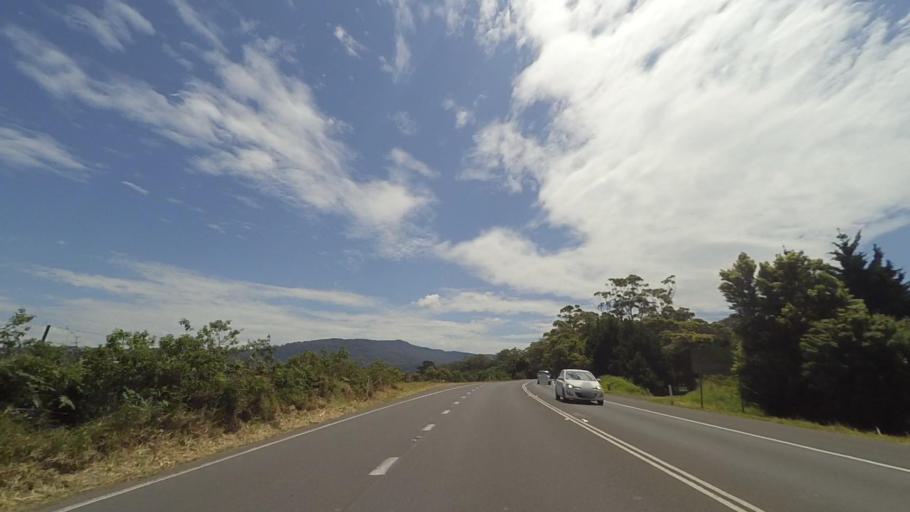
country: AU
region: New South Wales
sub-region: Kiama
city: Gerringong
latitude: -34.7433
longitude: 150.7726
